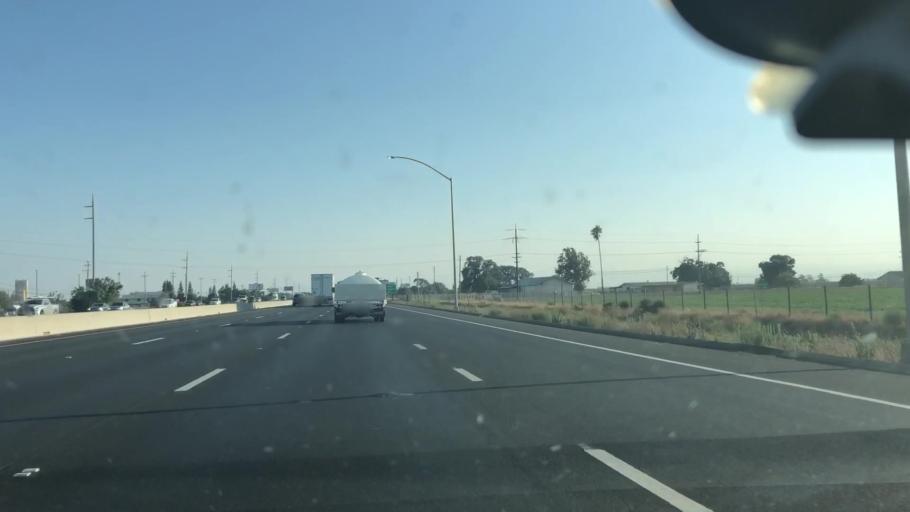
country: US
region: California
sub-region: San Joaquin County
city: French Camp
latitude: 37.8675
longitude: -121.2790
